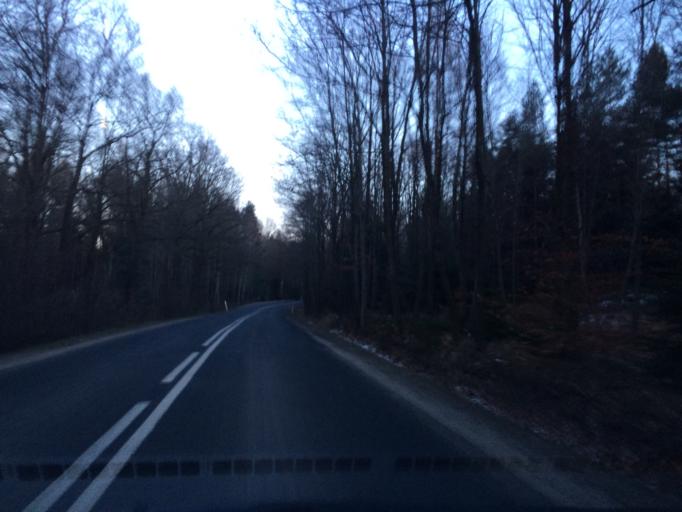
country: PL
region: Lower Silesian Voivodeship
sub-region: Powiat zlotoryjski
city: Olszanica
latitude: 51.1212
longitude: 15.7421
